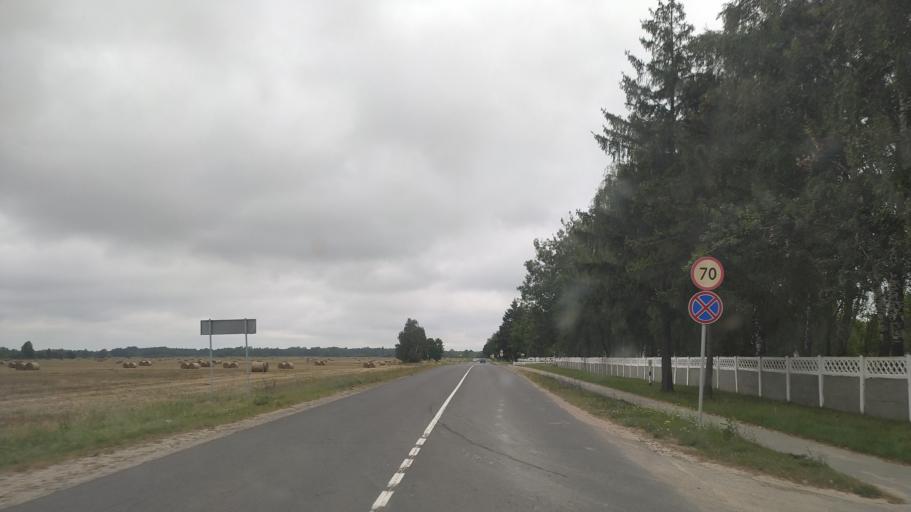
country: BY
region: Brest
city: Byaroza
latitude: 52.5533
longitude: 24.9293
